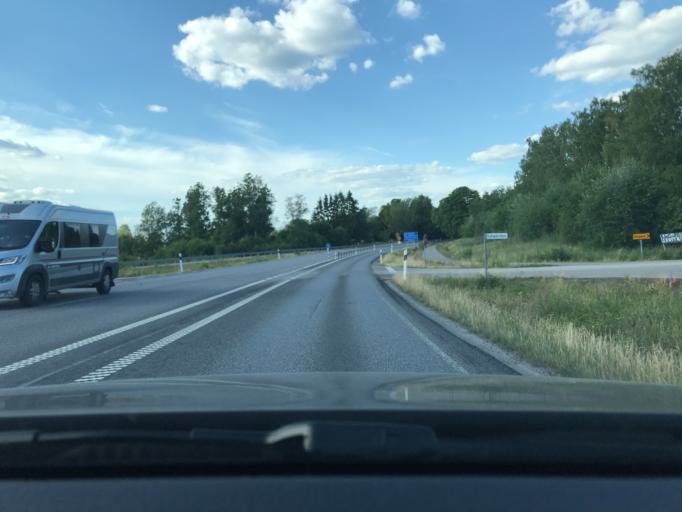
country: SE
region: Kronoberg
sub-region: Vaxjo Kommun
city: Vaexjoe
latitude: 56.9367
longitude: 14.8679
